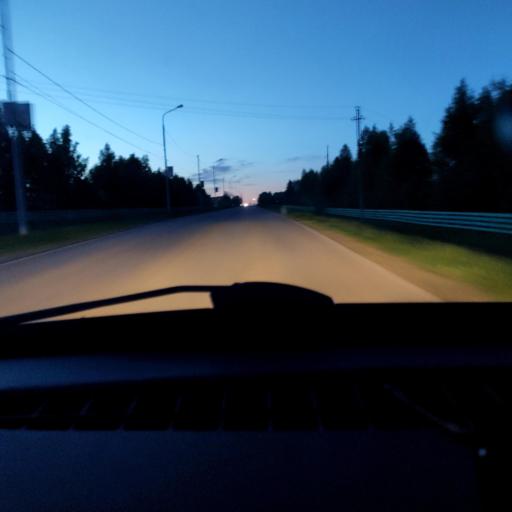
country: RU
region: Bashkortostan
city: Karmaskaly
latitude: 54.3762
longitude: 56.1760
